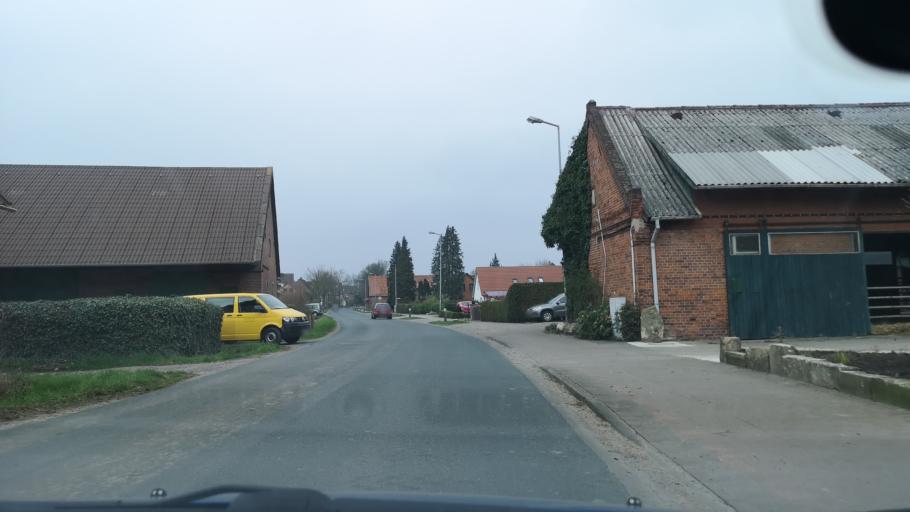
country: DE
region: Lower Saxony
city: Neustadt am Rubenberge
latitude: 52.5003
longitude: 9.5278
